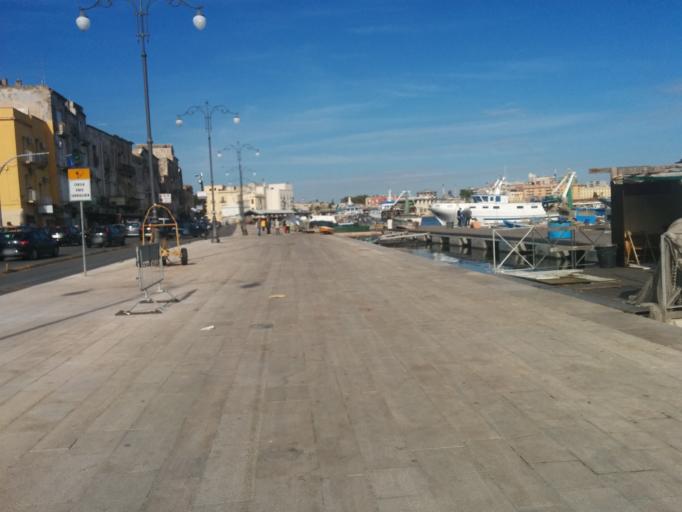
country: IT
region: Apulia
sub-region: Provincia di Taranto
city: Statte
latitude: 40.4775
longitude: 17.2299
